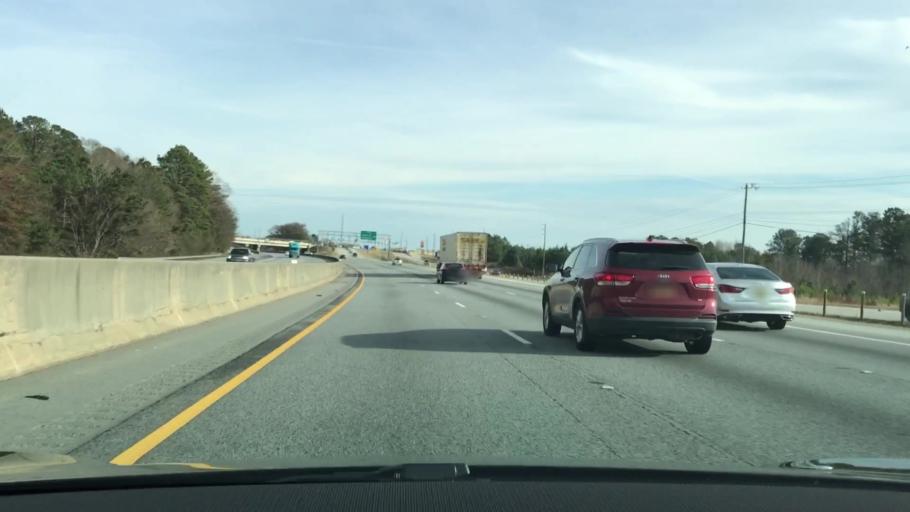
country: US
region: Georgia
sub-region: Newton County
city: Porterdale
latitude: 33.6169
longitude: -83.9266
